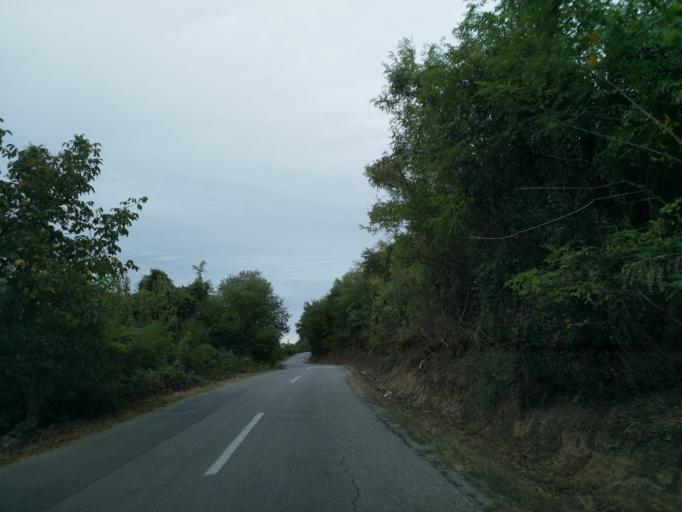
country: RS
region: Central Serbia
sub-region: Pomoravski Okrug
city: Paracin
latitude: 43.8558
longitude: 21.3245
